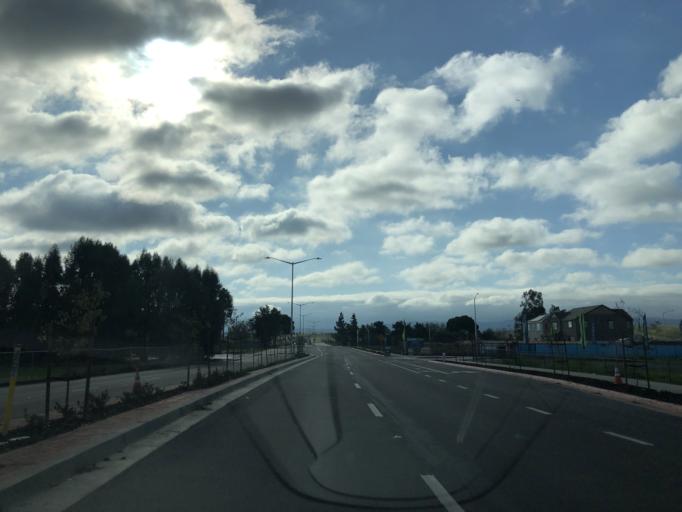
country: US
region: California
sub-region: Contra Costa County
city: Oakley
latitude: 37.9567
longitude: -121.7508
